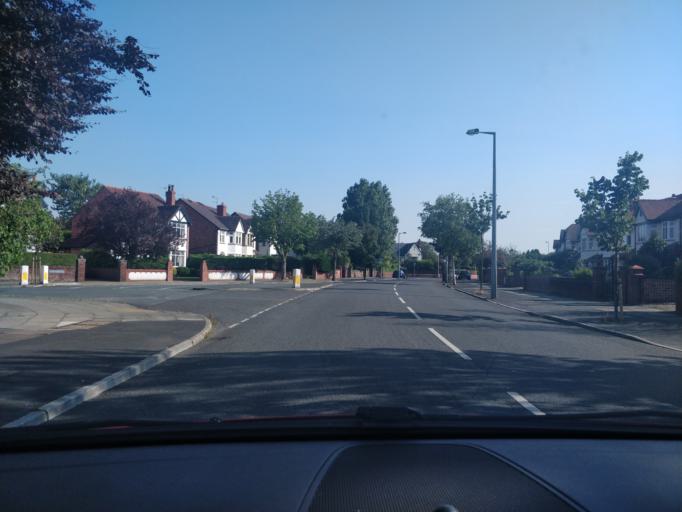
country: GB
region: England
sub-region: Sefton
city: Southport
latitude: 53.6551
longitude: -2.9745
